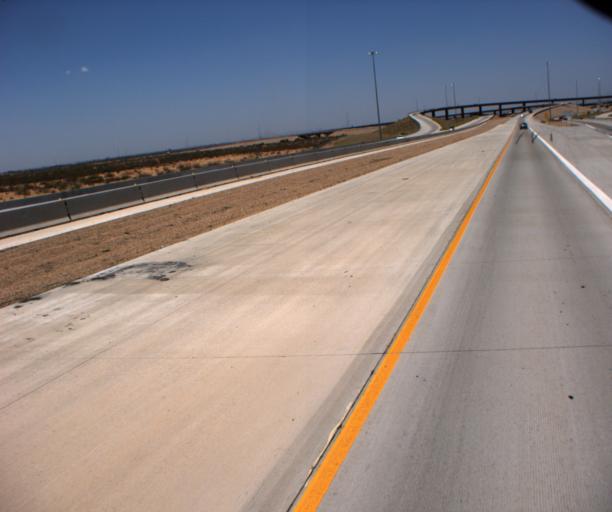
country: US
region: Arizona
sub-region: Maricopa County
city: Queen Creek
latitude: 33.3242
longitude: -111.6450
